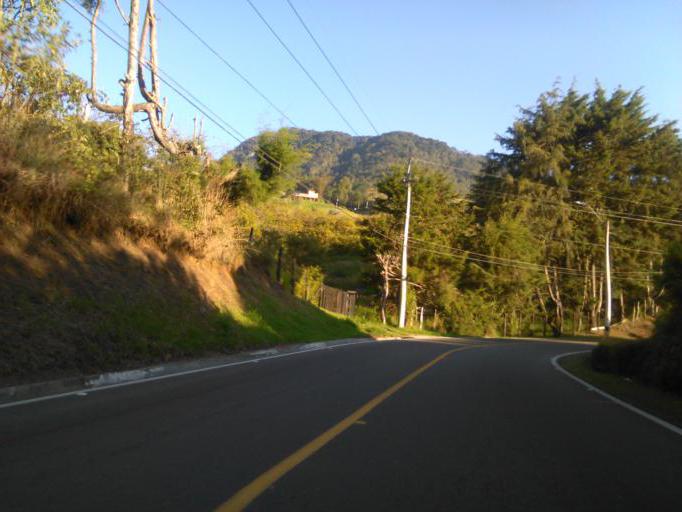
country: CO
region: Antioquia
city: La Ceja
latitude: 6.0129
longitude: -75.4054
